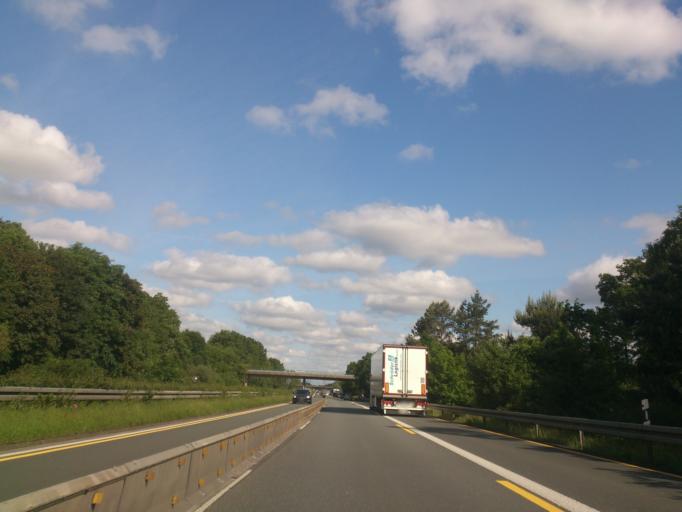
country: DE
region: North Rhine-Westphalia
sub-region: Regierungsbezirk Detmold
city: Hovelhof
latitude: 51.8301
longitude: 8.6956
